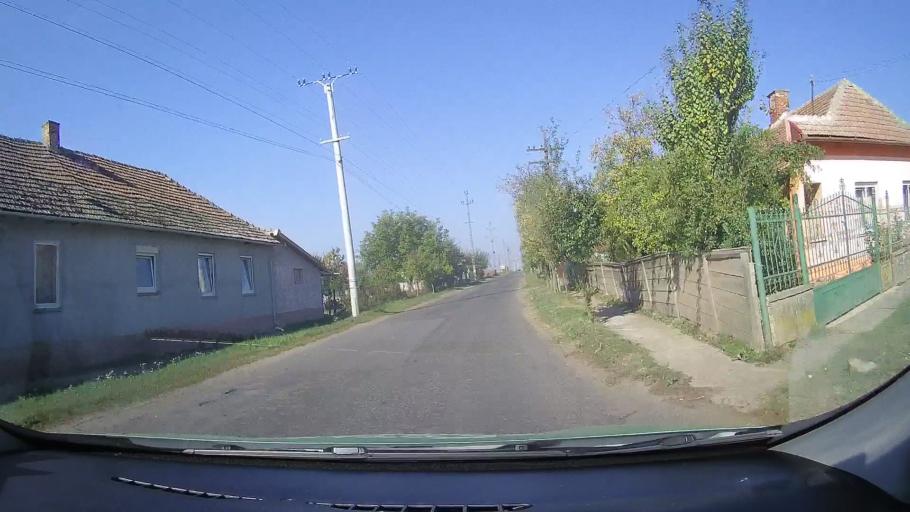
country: RO
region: Satu Mare
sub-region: Comuna Petresti
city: Petresti
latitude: 47.6087
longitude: 22.3572
